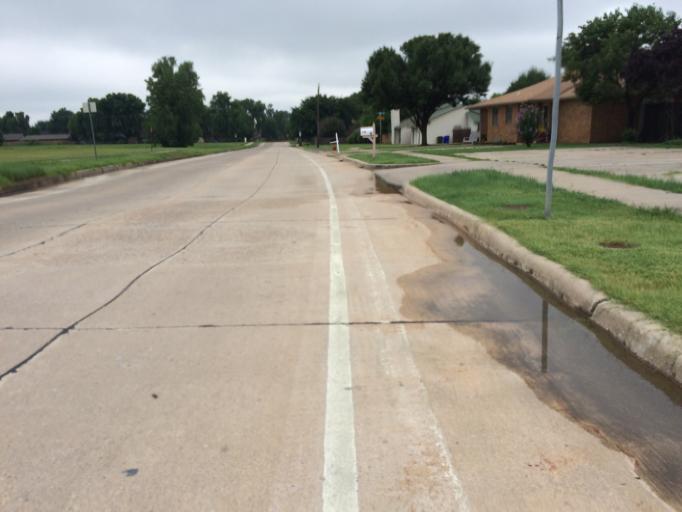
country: US
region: Oklahoma
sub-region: Cleveland County
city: Hall Park
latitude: 35.2132
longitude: -97.4132
